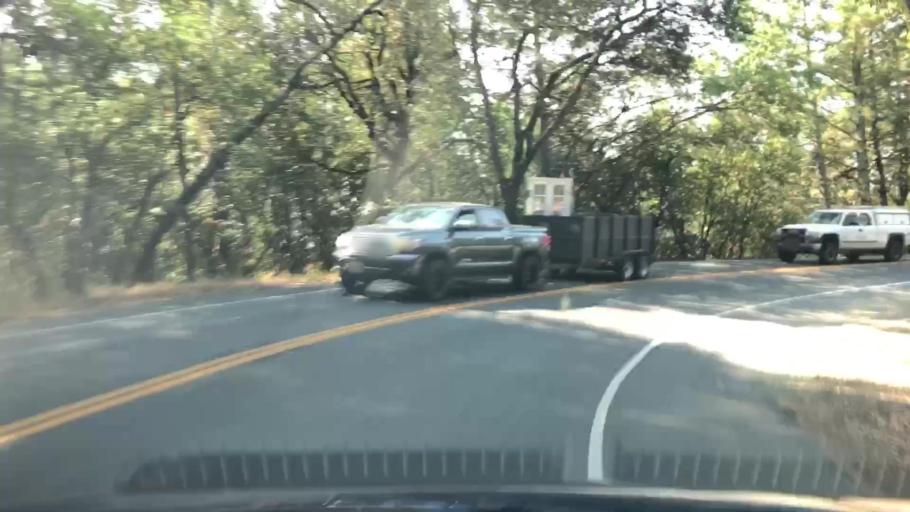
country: US
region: California
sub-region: Napa County
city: Calistoga
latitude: 38.6416
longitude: -122.5918
